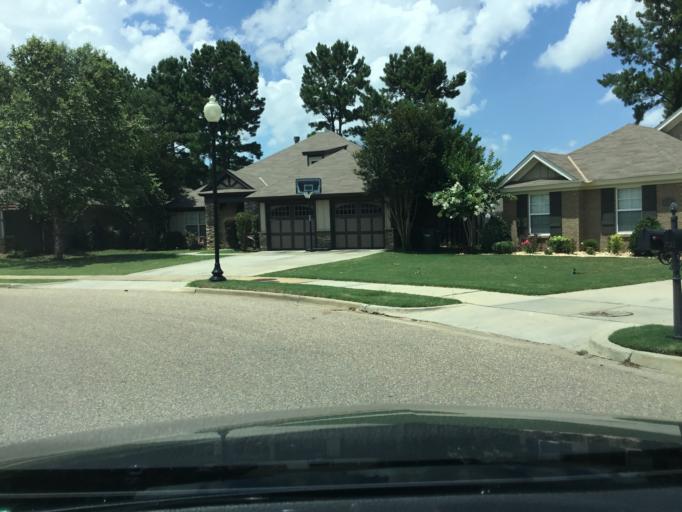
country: US
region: Alabama
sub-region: Montgomery County
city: Pike Road
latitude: 32.3407
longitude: -86.0812
